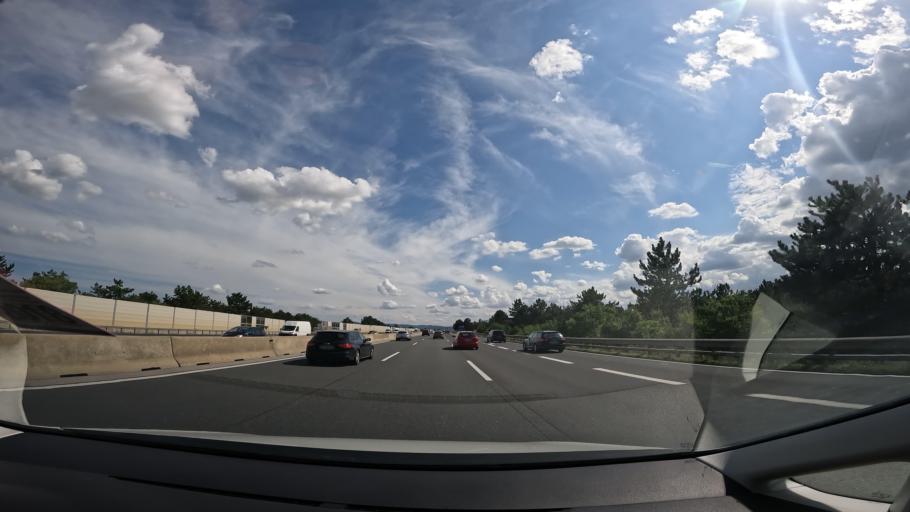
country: AT
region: Lower Austria
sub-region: Politischer Bezirk Wiener Neustadt
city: Theresienfeld
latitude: 47.8108
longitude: 16.1982
